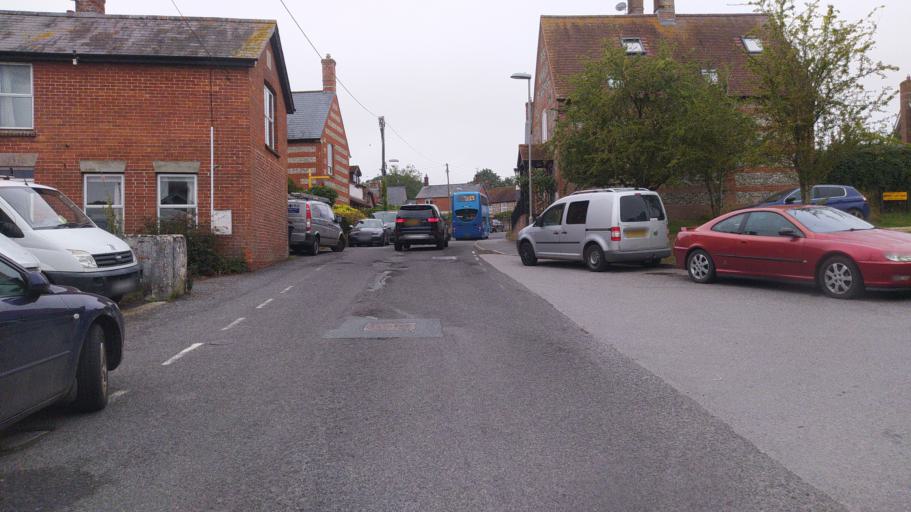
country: GB
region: England
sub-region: Wiltshire
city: Bower Chalke
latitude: 50.9532
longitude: -2.0031
